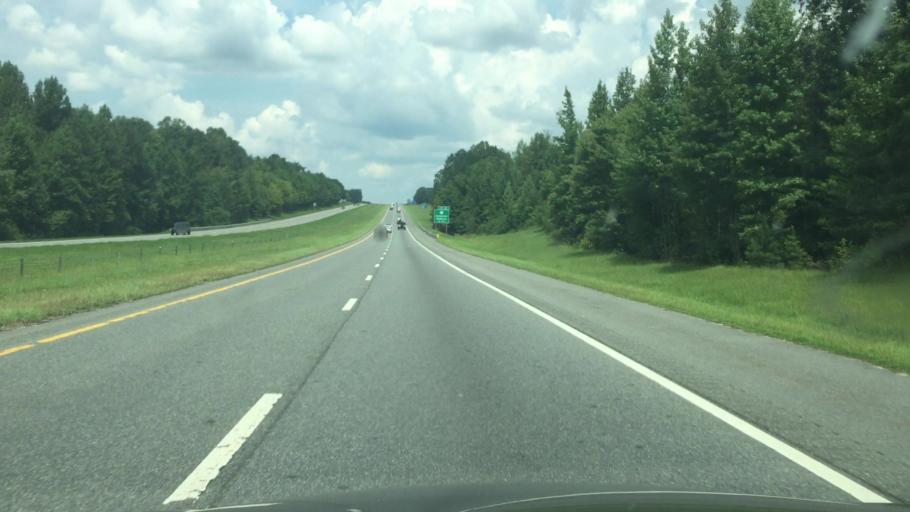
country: US
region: North Carolina
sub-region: Montgomery County
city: Biscoe
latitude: 35.5231
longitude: -79.7840
